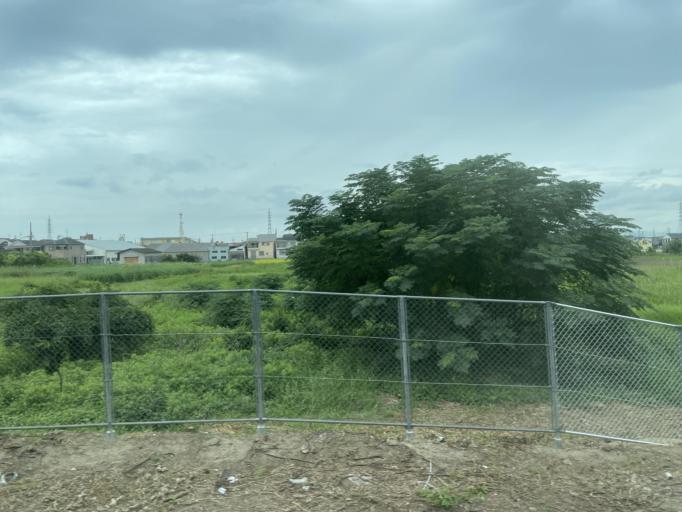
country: JP
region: Osaka
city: Izumi
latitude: 34.4728
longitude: 135.4127
